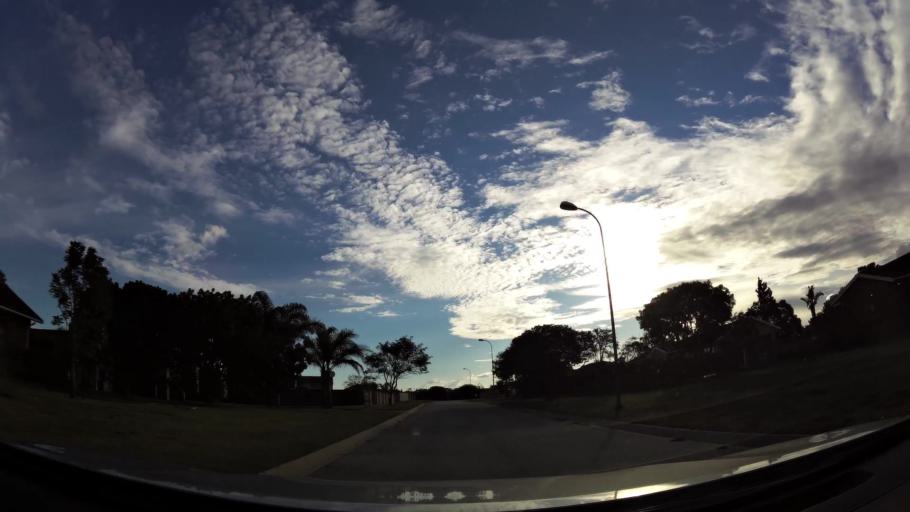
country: ZA
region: Eastern Cape
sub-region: Nelson Mandela Bay Metropolitan Municipality
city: Port Elizabeth
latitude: -33.9564
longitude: 25.4944
